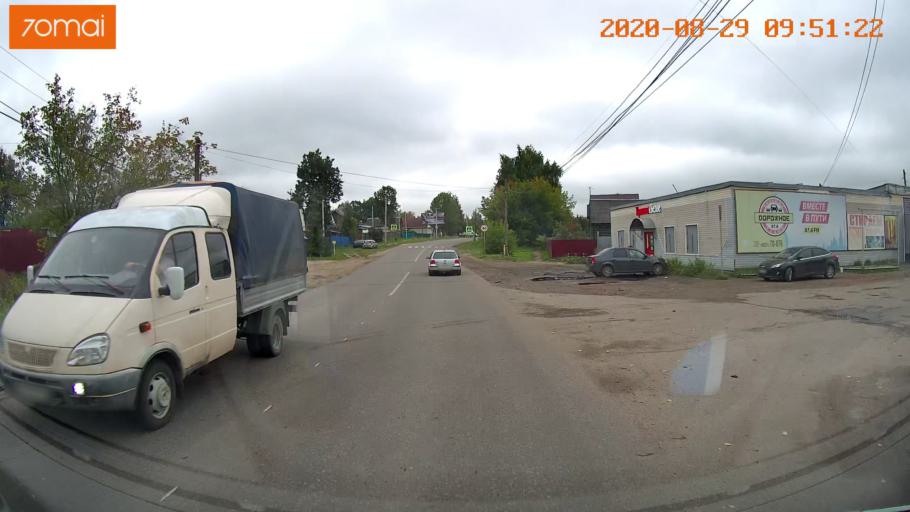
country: RU
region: Ivanovo
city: Kineshma
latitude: 57.4300
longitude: 42.1976
